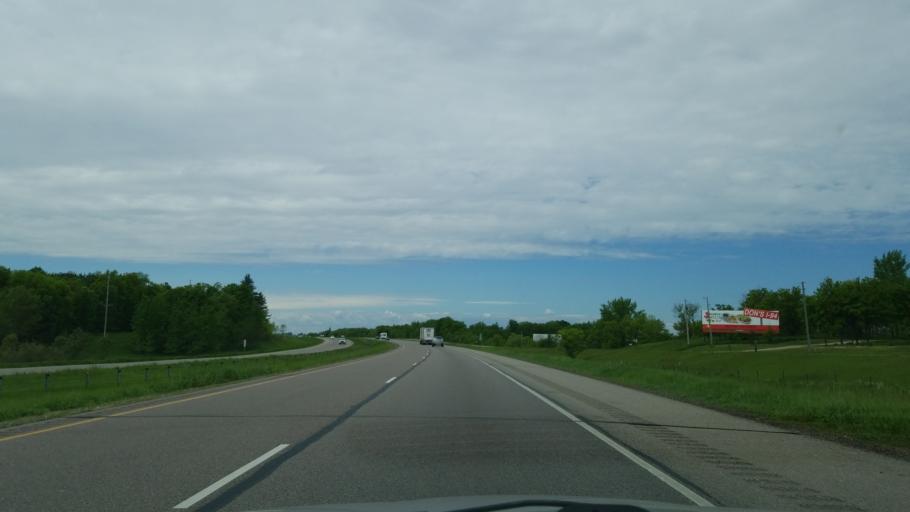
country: US
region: Minnesota
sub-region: Stearns County
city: Albany
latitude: 45.6148
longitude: -94.5121
